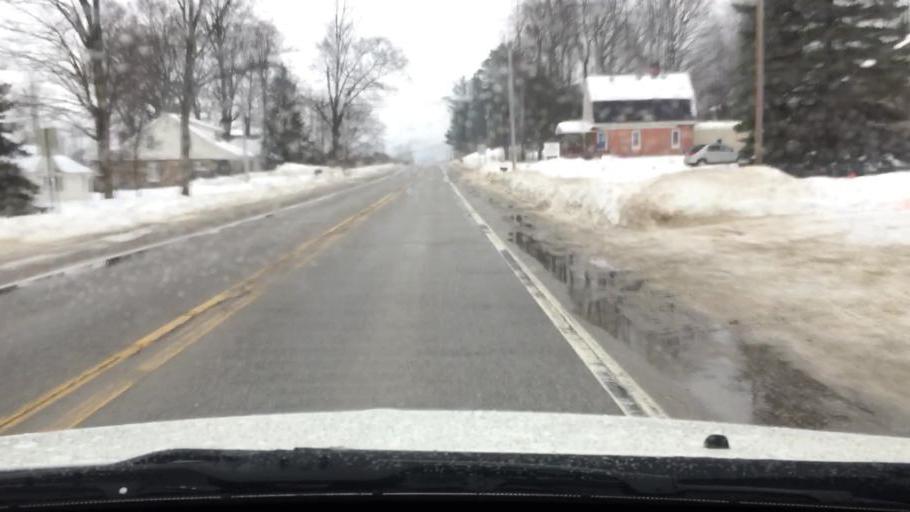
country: US
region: Michigan
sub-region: Charlevoix County
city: East Jordan
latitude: 45.1451
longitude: -85.1398
